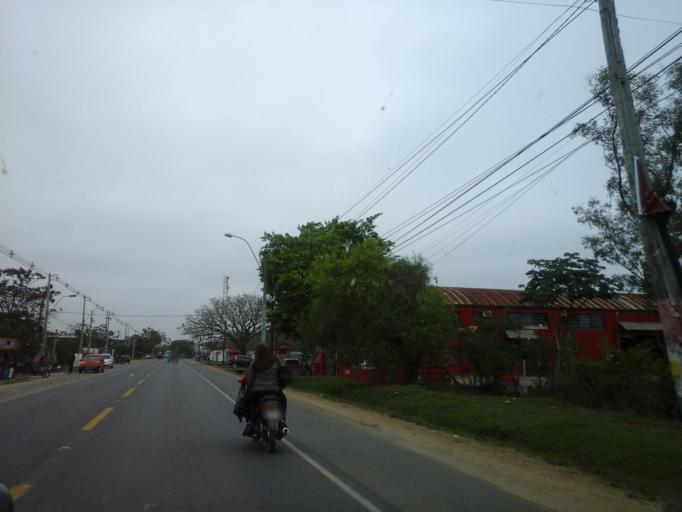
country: PY
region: Neembucu
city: Pilar
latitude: -26.8460
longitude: -58.2928
